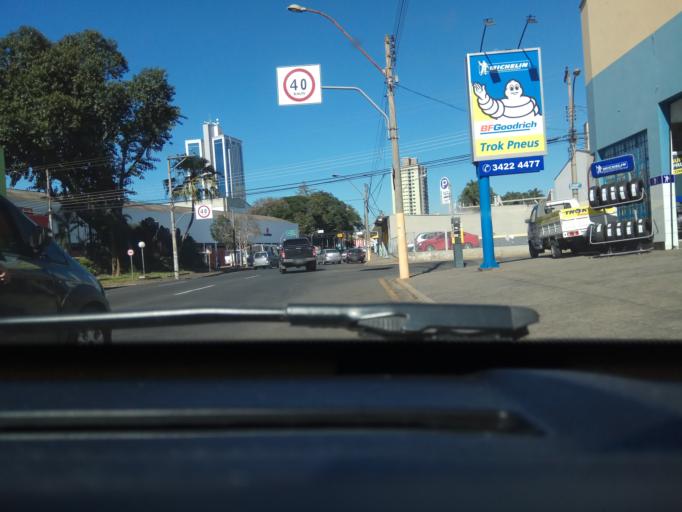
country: BR
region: Sao Paulo
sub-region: Piracicaba
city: Piracicaba
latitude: -22.7325
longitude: -47.6492
